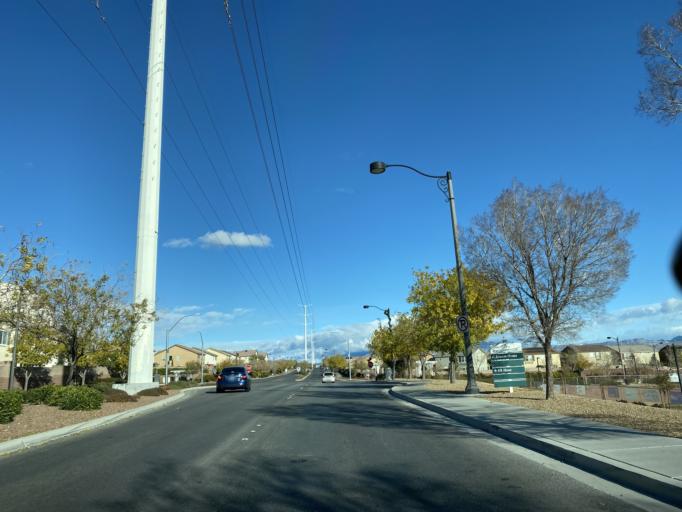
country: US
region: Nevada
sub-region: Clark County
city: Summerlin South
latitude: 36.2873
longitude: -115.3287
